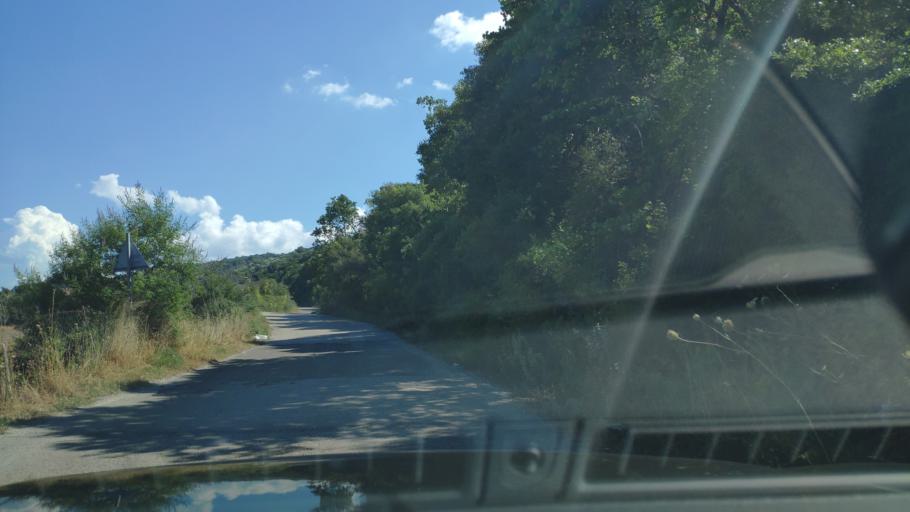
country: GR
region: West Greece
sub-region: Nomos Aitolias kai Akarnanias
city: Katouna
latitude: 38.8218
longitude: 21.1030
